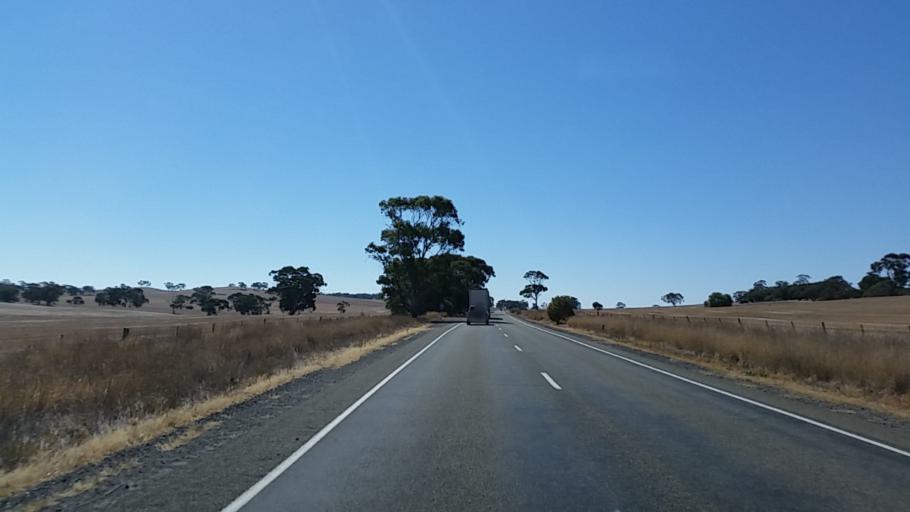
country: AU
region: South Australia
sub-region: Clare and Gilbert Valleys
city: Clare
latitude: -34.0501
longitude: 138.7972
